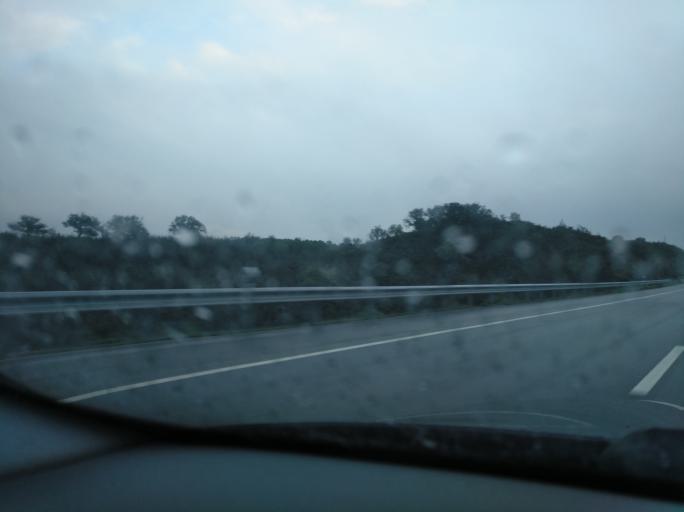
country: PT
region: Faro
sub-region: Alcoutim
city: Alcoutim
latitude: 37.3662
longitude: -7.5224
